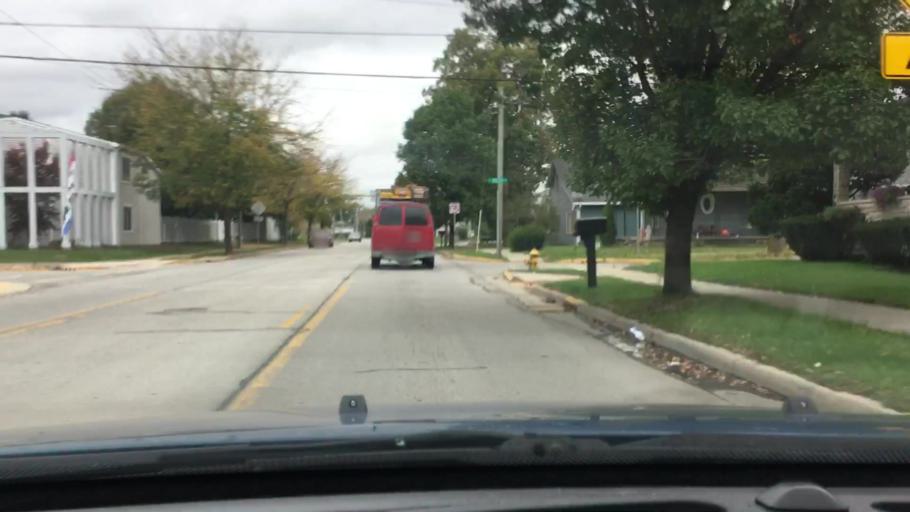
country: US
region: Indiana
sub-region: Jay County
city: Portland
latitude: 40.4259
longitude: -84.9777
